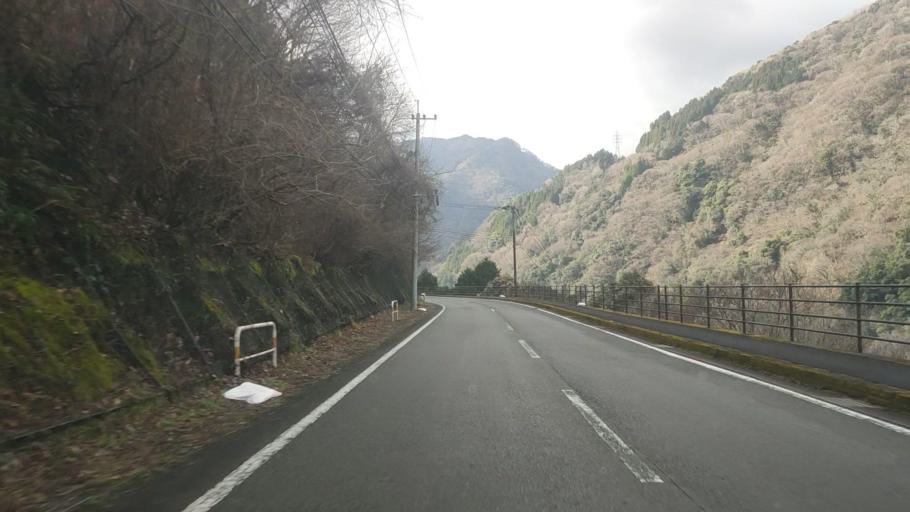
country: JP
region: Kumamoto
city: Hitoyoshi
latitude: 32.4066
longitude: 130.8276
